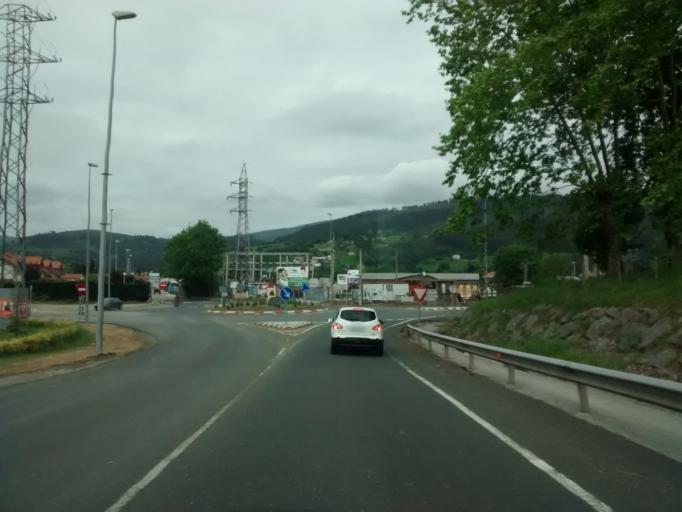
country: ES
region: Cantabria
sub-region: Provincia de Cantabria
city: Los Corrales de Buelna
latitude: 43.2518
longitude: -4.0710
